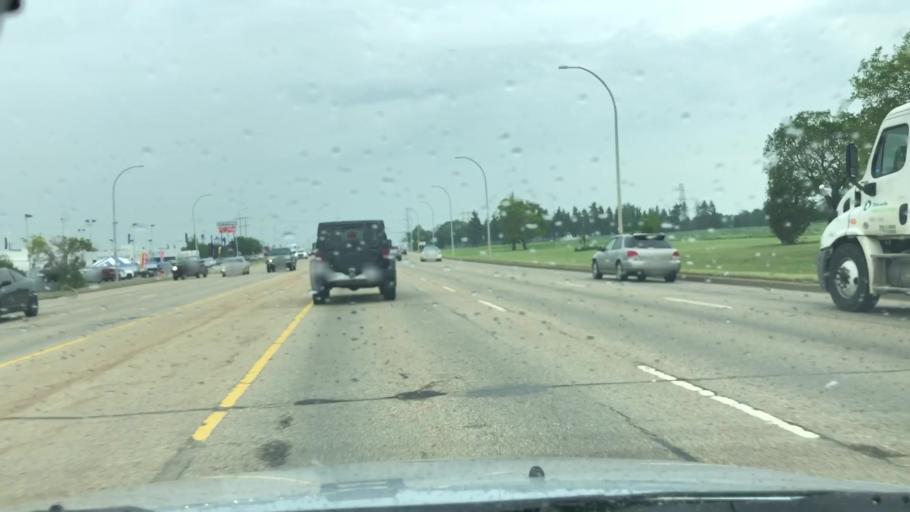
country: CA
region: Alberta
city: St. Albert
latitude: 53.6090
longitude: -113.5863
